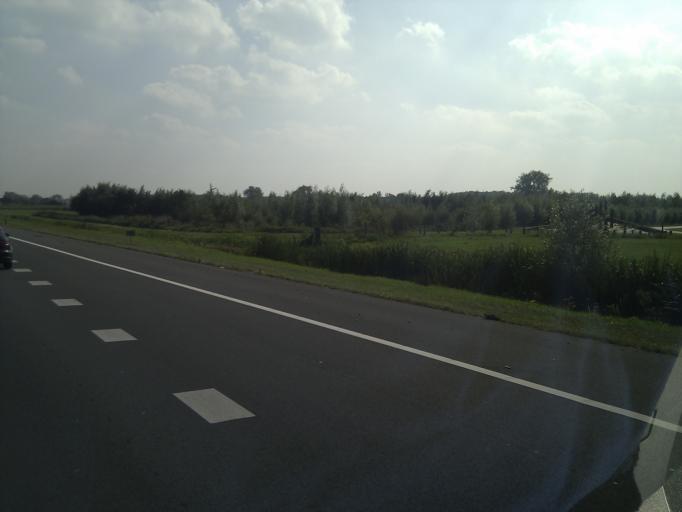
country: NL
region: Gelderland
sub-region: Gemeente Culemborg
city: Culemborg
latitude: 51.9264
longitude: 5.1668
